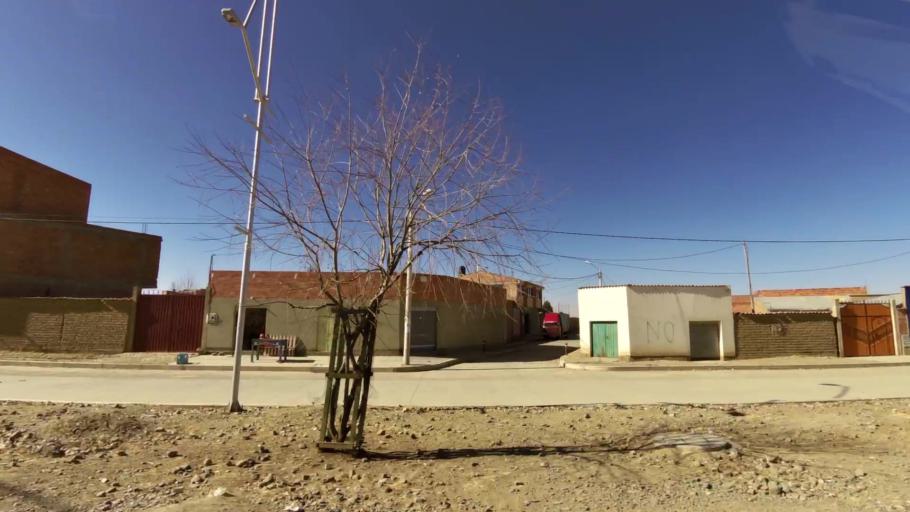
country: BO
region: La Paz
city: La Paz
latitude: -16.5312
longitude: -68.2350
